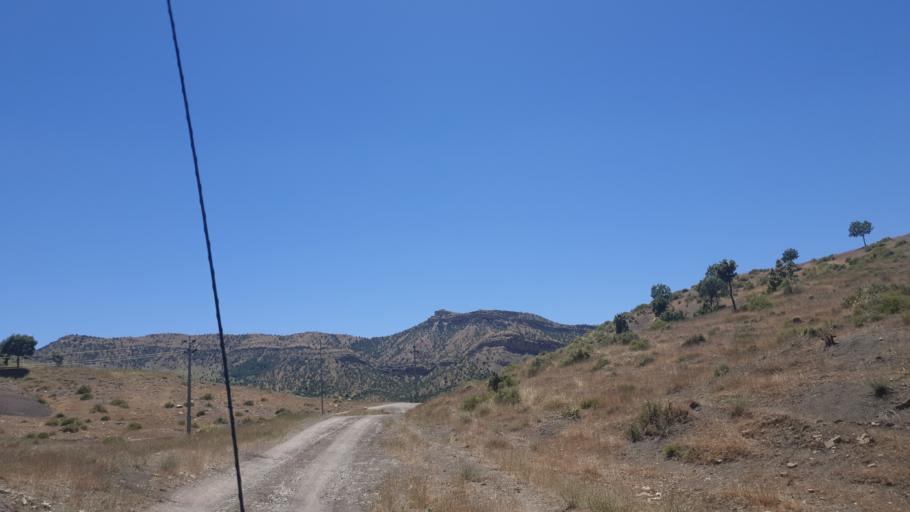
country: IQ
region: Arbil
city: Nahiyat Hiran
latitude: 36.2008
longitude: 44.4229
